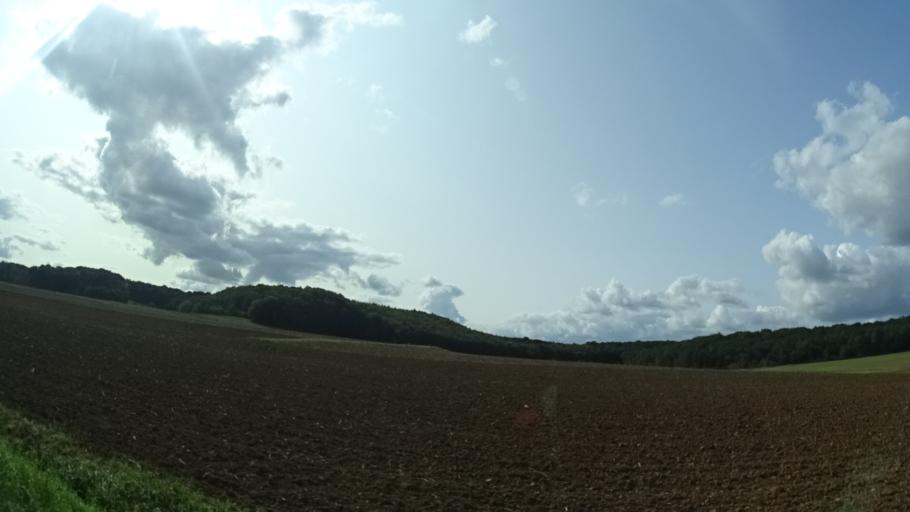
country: DE
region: Bavaria
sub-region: Regierungsbezirk Unterfranken
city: Greussenheim
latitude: 49.8243
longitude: 9.7772
